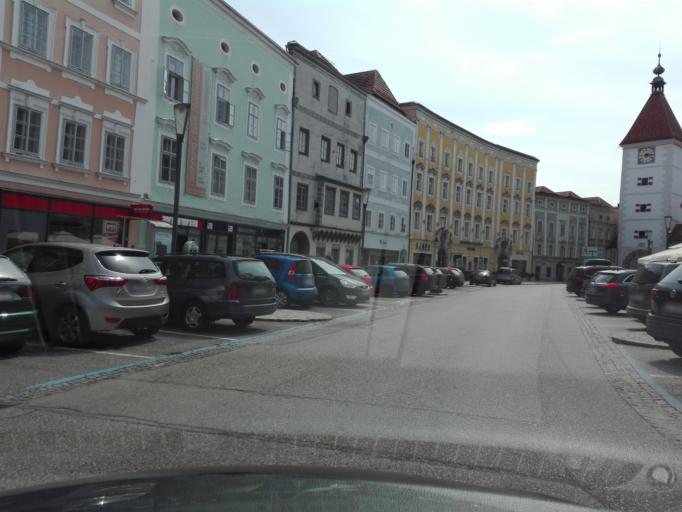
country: AT
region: Upper Austria
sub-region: Wels-Land
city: Thalheim bei Wels
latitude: 48.1564
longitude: 14.0242
